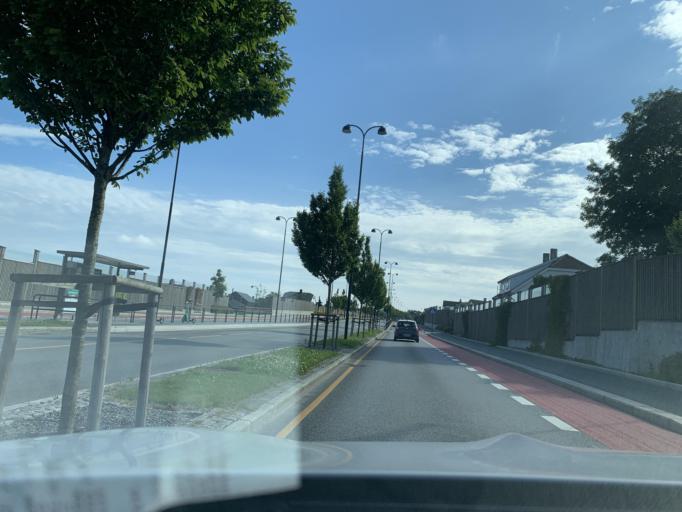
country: NO
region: Rogaland
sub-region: Stavanger
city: Stavanger
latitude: 58.9319
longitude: 5.7385
